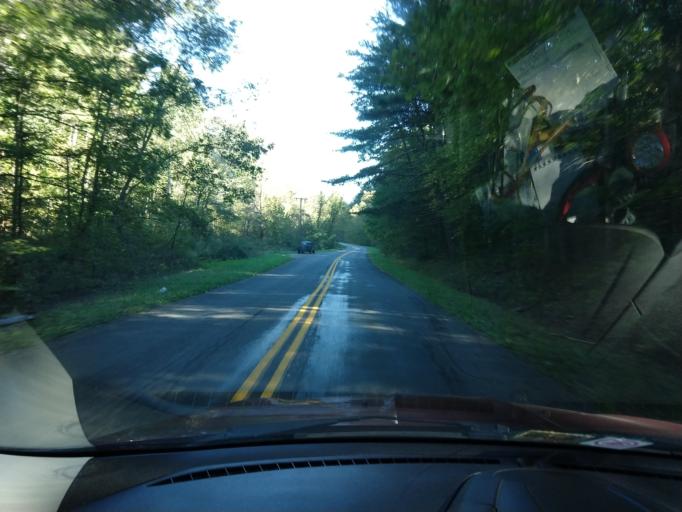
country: US
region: Virginia
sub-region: Alleghany County
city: Clifton Forge
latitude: 37.8316
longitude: -79.8410
